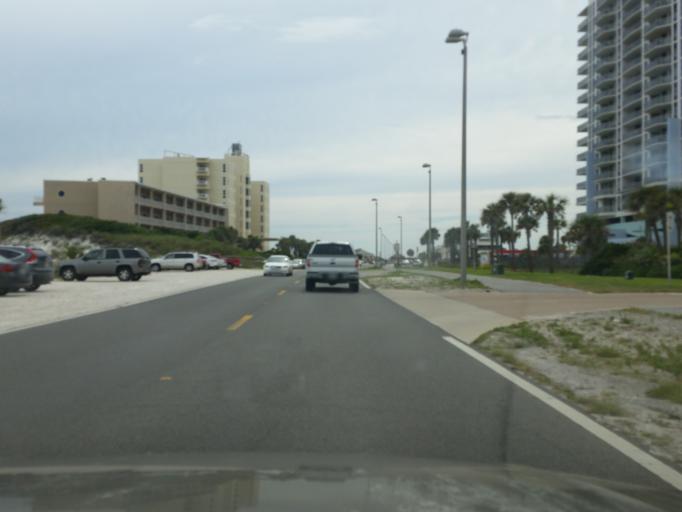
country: US
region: Florida
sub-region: Santa Rosa County
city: Gulf Breeze
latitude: 30.3281
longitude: -87.1614
